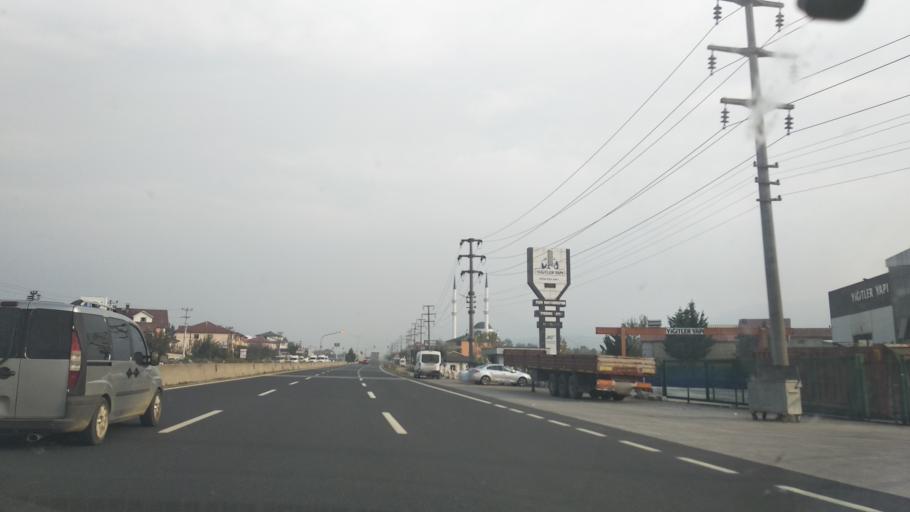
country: TR
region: Duzce
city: Duzce
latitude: 40.8051
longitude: 31.2337
